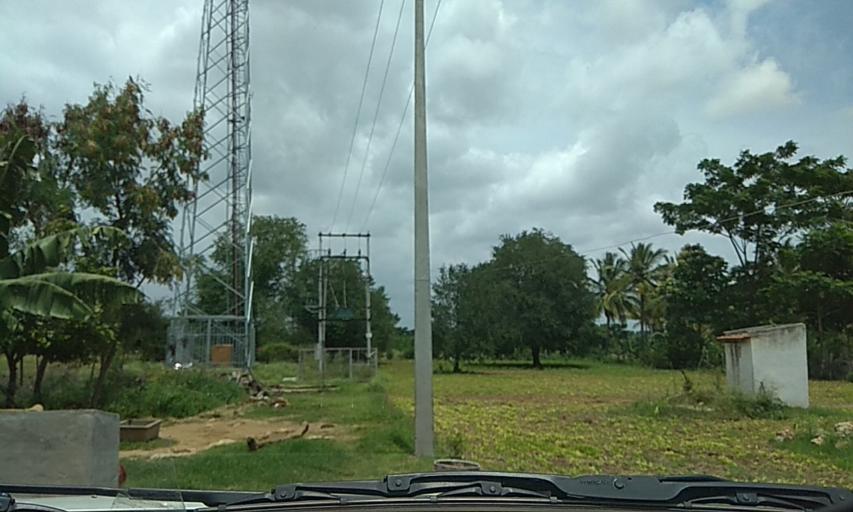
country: IN
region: Karnataka
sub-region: Chamrajnagar
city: Gundlupet
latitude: 11.8879
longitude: 76.6981
